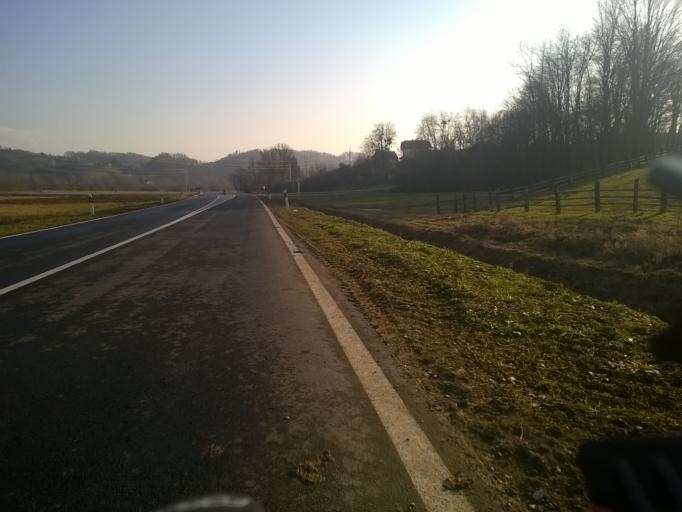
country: HR
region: Krapinsko-Zagorska
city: Zabok
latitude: 46.0385
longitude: 15.9179
